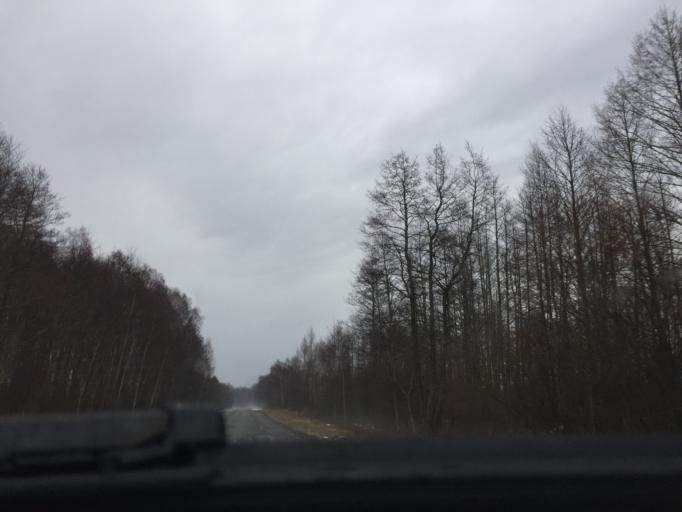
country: EE
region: Saare
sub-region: Orissaare vald
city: Orissaare
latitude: 58.5702
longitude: 23.0343
